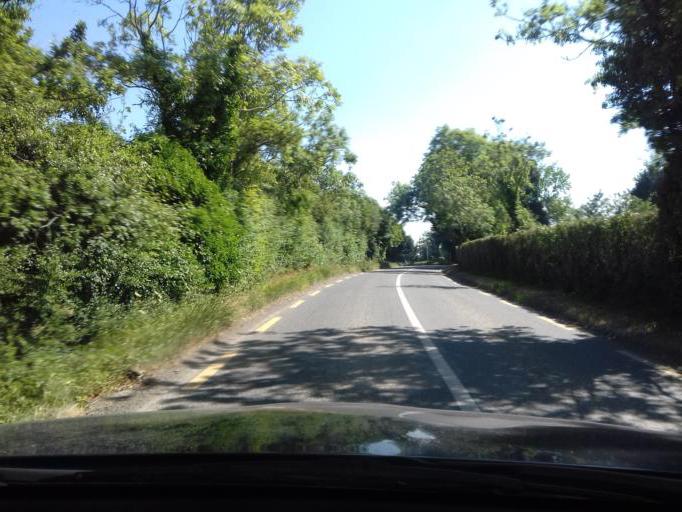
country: IE
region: Leinster
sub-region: An Mhi
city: Stamullin
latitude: 53.5446
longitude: -6.2723
